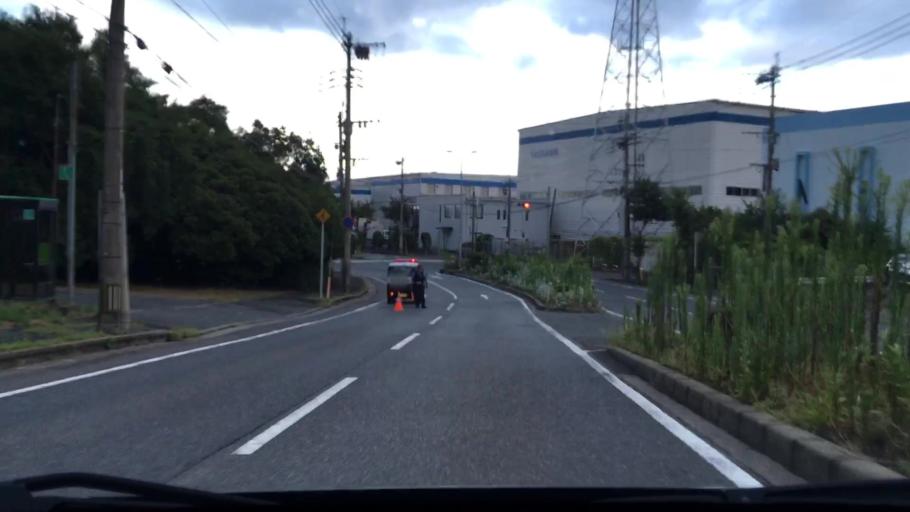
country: JP
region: Yamaguchi
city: Shimonoseki
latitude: 33.8864
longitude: 130.9841
